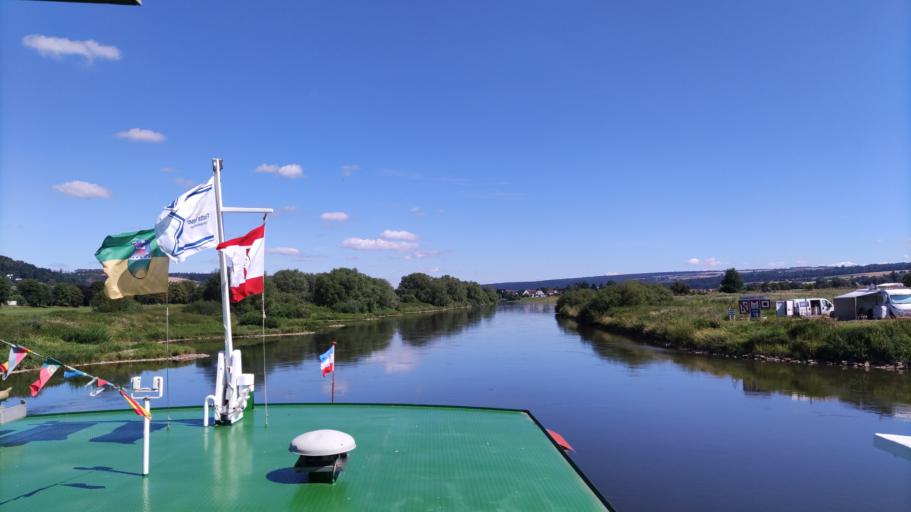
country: DE
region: North Rhine-Westphalia
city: Beverungen
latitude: 51.6508
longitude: 9.3748
